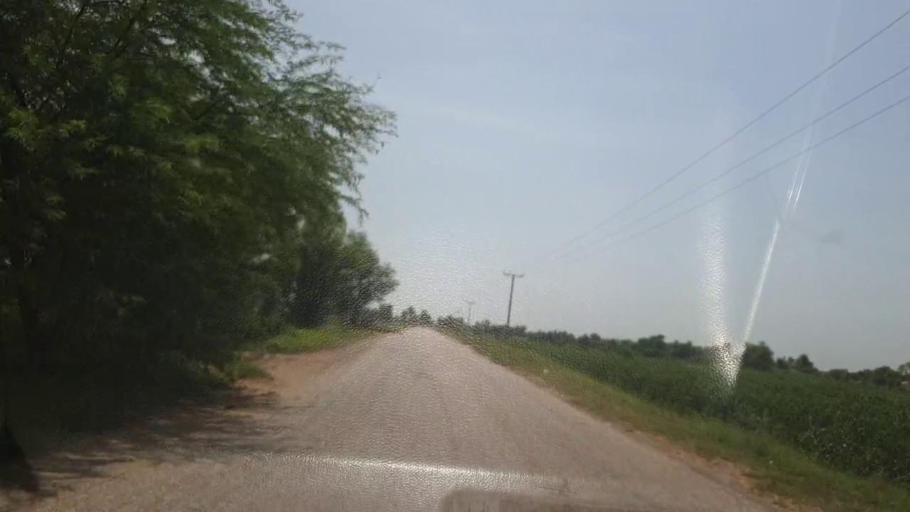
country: PK
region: Sindh
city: Kandiari
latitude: 27.0551
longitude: 68.5578
